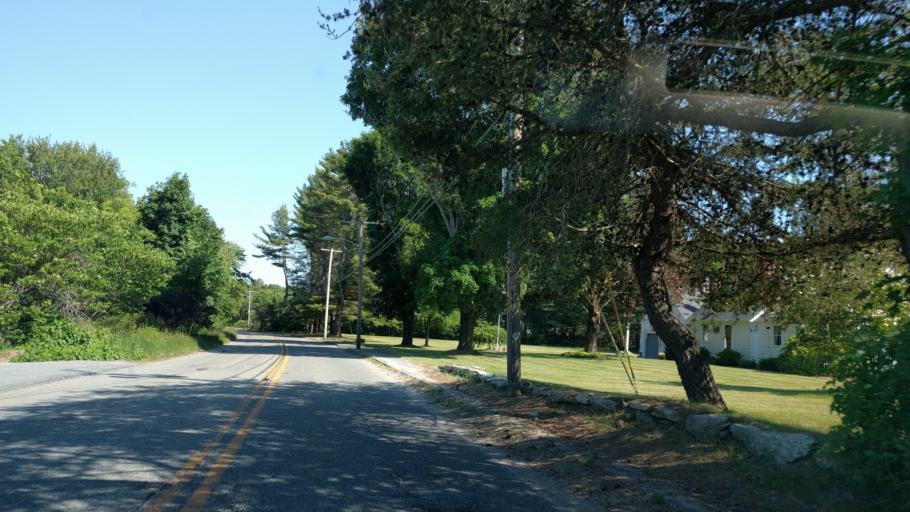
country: US
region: Massachusetts
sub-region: Worcester County
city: East Douglas
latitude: 42.0780
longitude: -71.7276
